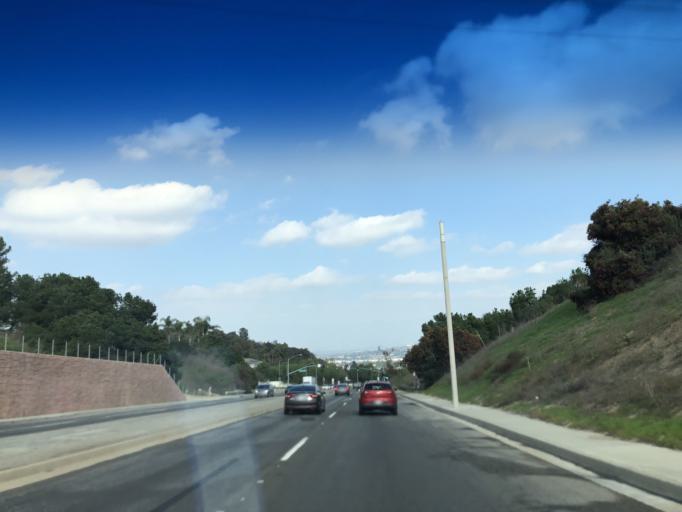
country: US
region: California
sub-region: Los Angeles County
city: Hacienda Heights
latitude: 33.9765
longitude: -117.9831
